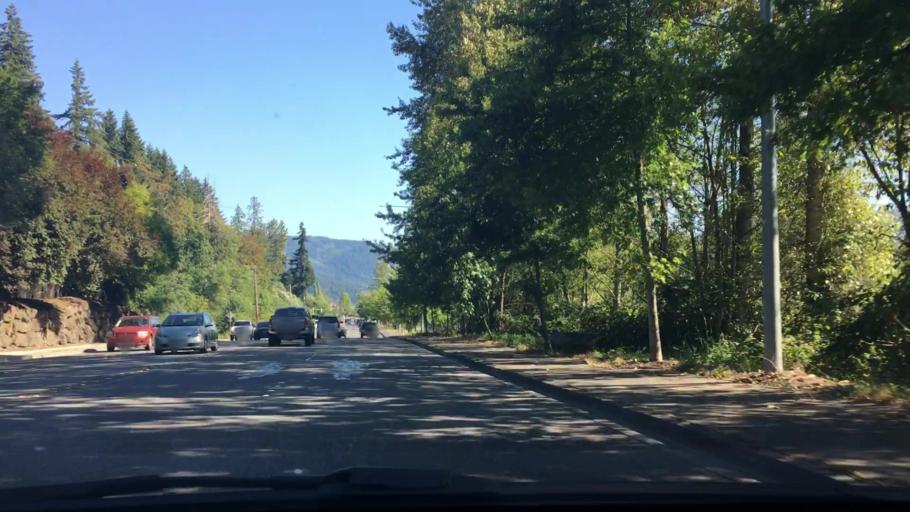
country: US
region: Washington
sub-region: King County
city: Issaquah
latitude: 47.5597
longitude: -122.0485
